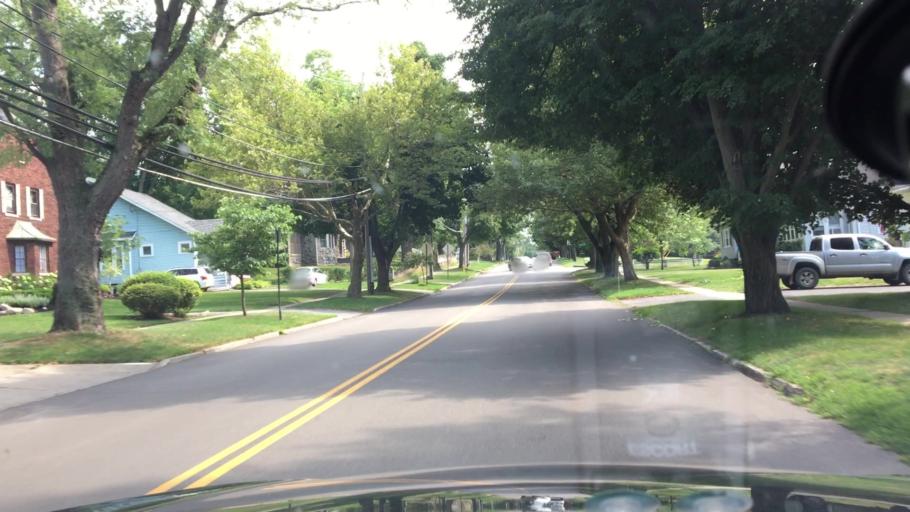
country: US
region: New York
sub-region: Erie County
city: Williamsville
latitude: 42.9667
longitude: -78.7437
